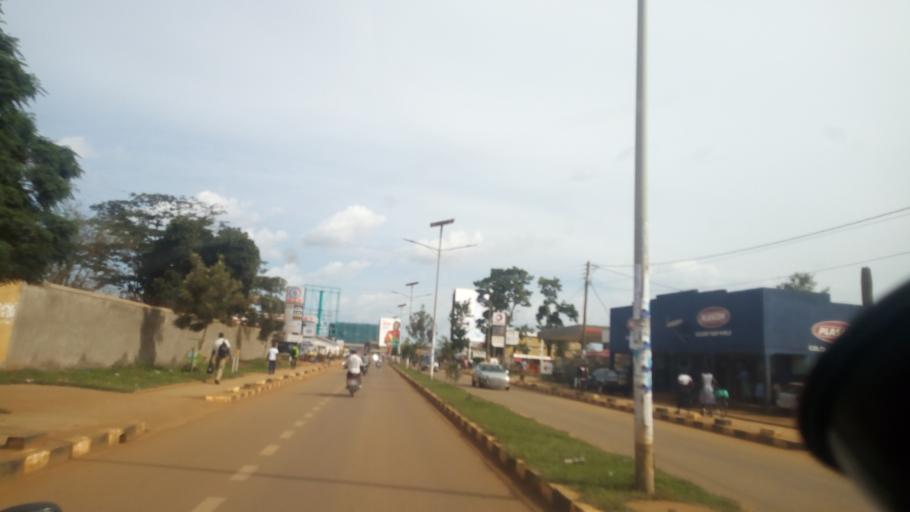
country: UG
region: Northern Region
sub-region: Lira District
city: Lira
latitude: 2.2353
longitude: 32.8931
